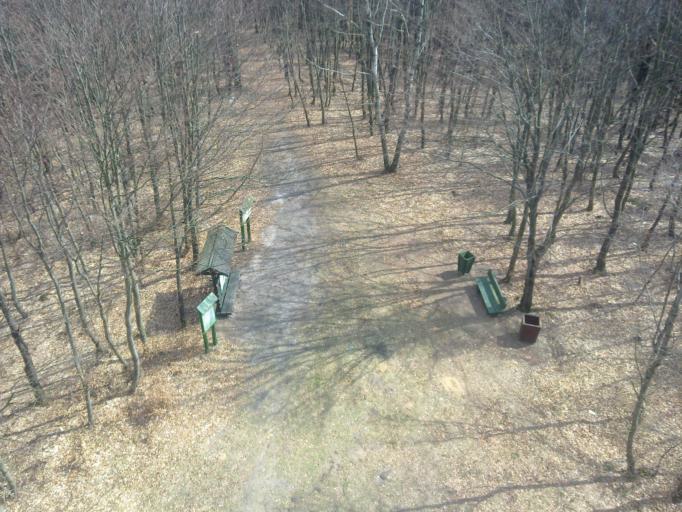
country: PL
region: Pomeranian Voivodeship
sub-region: Powiat bytowski
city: Tuchomie
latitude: 54.0893
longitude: 17.4077
